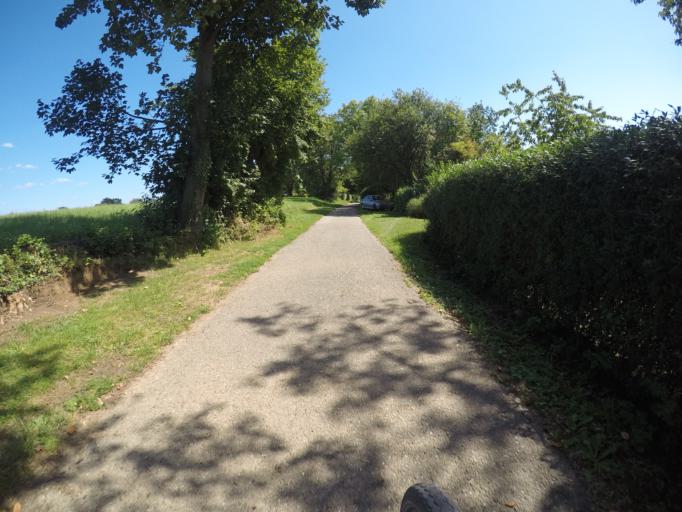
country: DE
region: Baden-Wuerttemberg
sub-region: Regierungsbezirk Stuttgart
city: Leinfelden-Echterdingen
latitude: 48.7083
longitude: 9.1893
